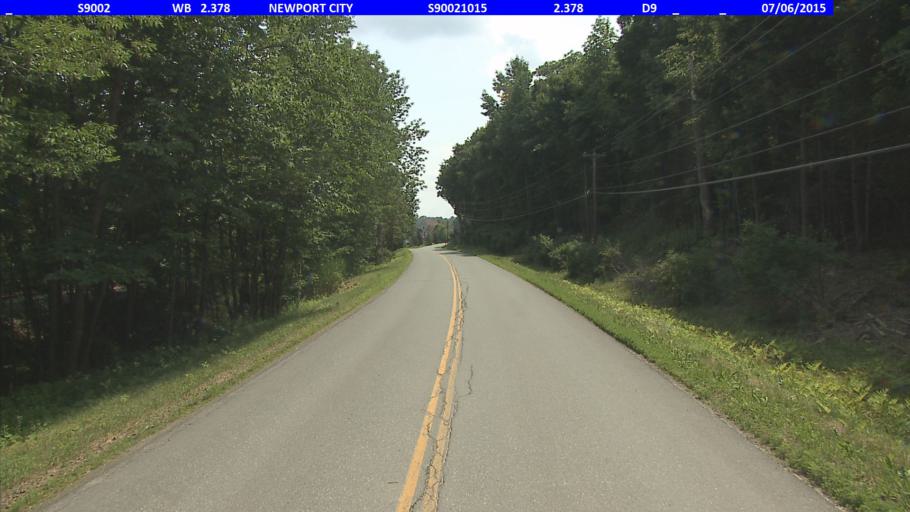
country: US
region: Vermont
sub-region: Orleans County
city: Newport
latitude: 44.9488
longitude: -72.2369
